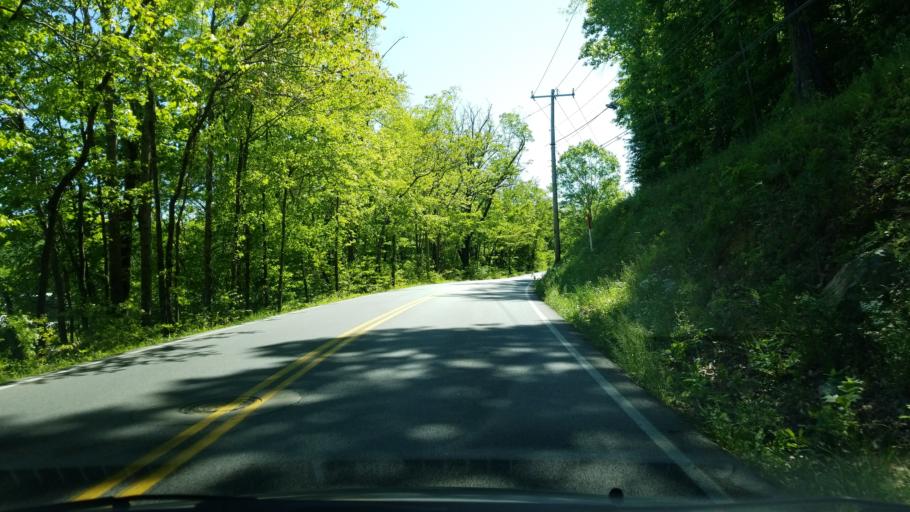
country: US
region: Tennessee
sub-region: Hamilton County
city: Falling Water
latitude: 35.1822
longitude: -85.2435
